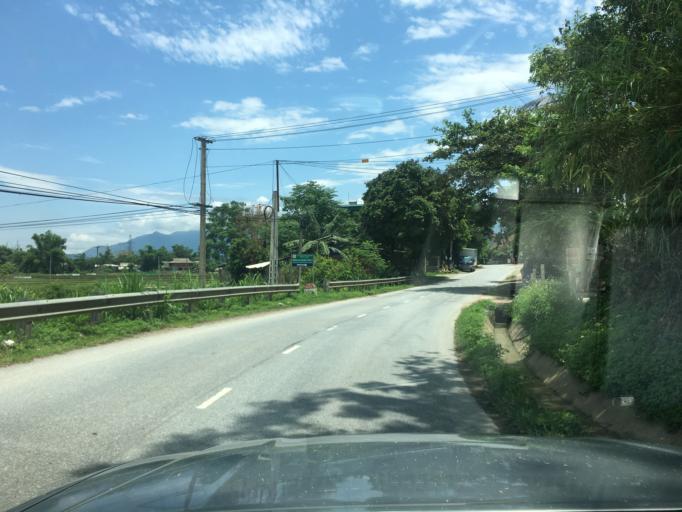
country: VN
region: Yen Bai
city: Son Thinh
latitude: 21.6274
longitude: 104.5081
